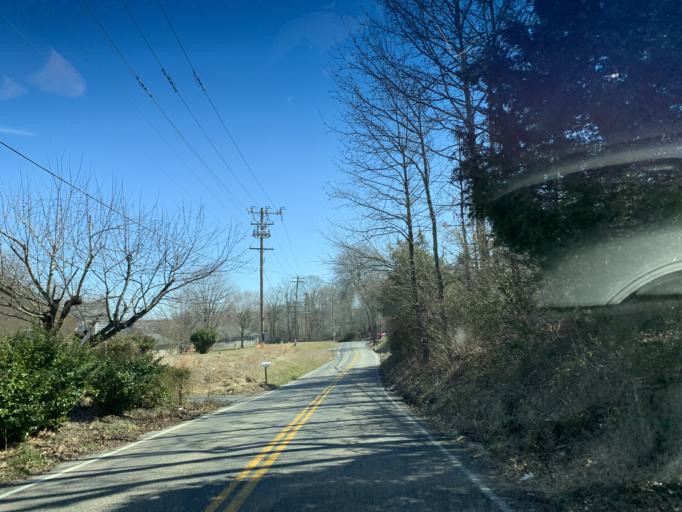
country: US
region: Maryland
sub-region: Cecil County
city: North East
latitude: 39.5992
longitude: -75.9590
